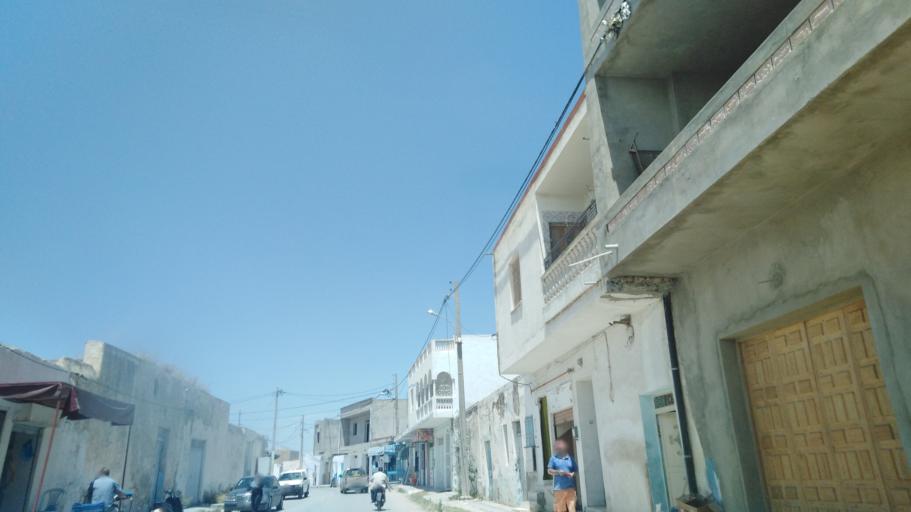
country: TN
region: Al Mahdiyah
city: Ksour Essaf
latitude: 35.4169
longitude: 10.9876
